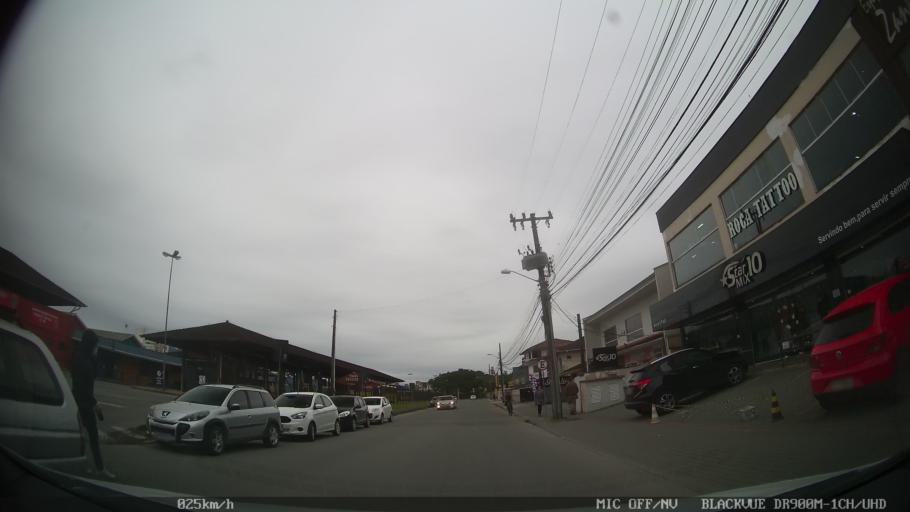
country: BR
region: Santa Catarina
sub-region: Joinville
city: Joinville
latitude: -26.2871
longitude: -48.9023
